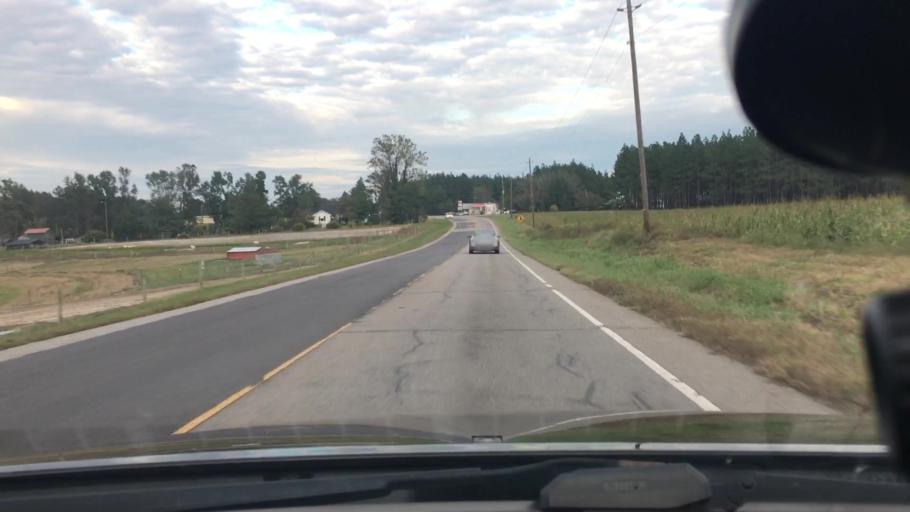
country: US
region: North Carolina
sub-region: Moore County
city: Carthage
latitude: 35.3609
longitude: -79.3240
